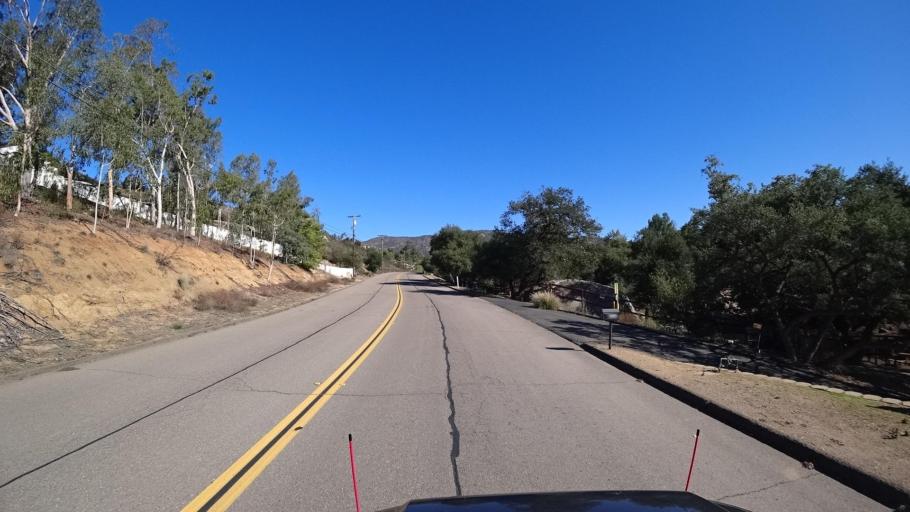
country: US
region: California
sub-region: San Diego County
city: Jamul
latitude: 32.7214
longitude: -116.8465
